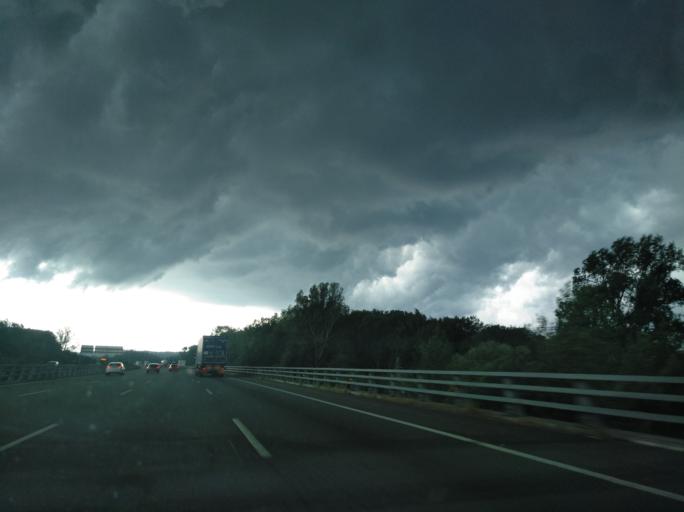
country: ES
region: Catalonia
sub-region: Provincia de Girona
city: Salt
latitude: 41.9831
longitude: 2.7815
